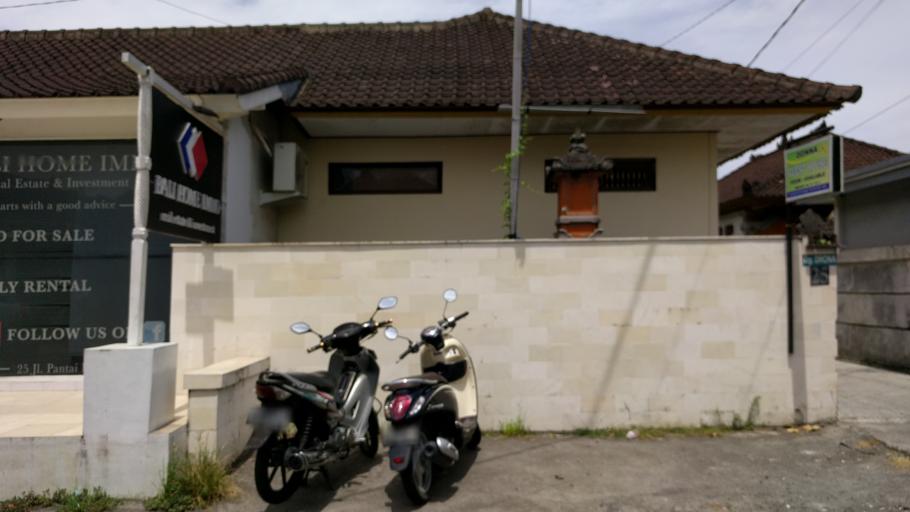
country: ID
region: Bali
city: Banjar Gunungpande
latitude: -8.6596
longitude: 115.1469
